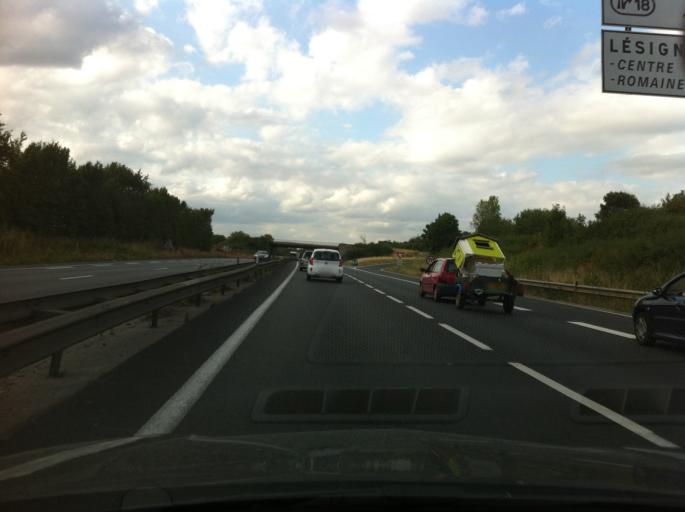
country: FR
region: Ile-de-France
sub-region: Departement de Seine-et-Marne
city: Lesigny
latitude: 48.7470
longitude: 2.6137
